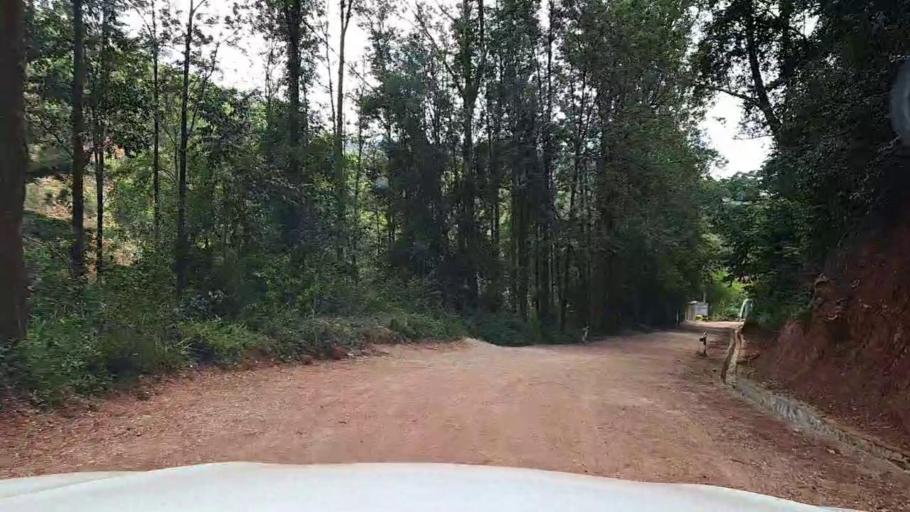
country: BI
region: Ngozi
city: Ngozi
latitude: -2.8145
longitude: 29.7282
